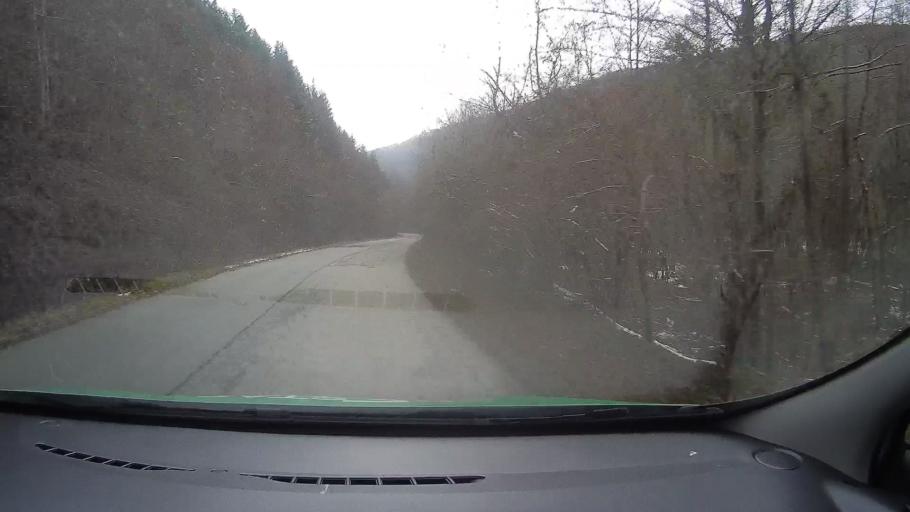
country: RO
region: Hunedoara
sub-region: Comuna Balsa
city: Balsa
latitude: 46.0056
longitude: 23.1507
